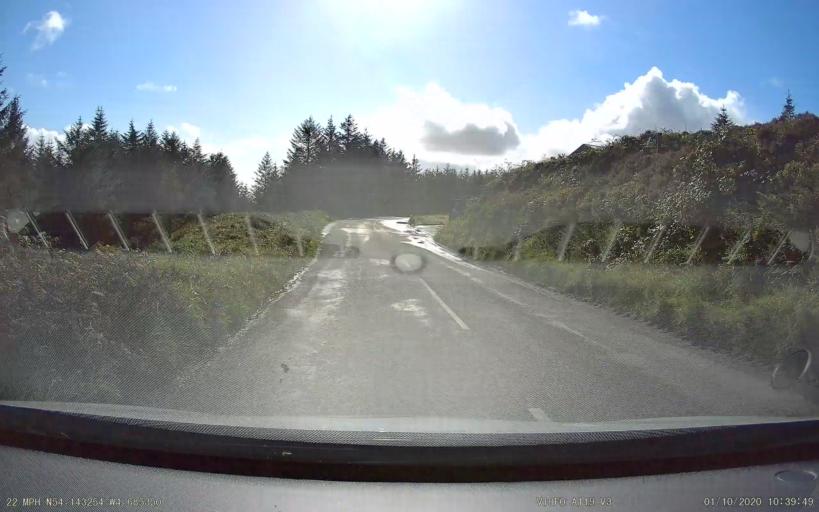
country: IM
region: Castletown
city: Castletown
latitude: 54.1433
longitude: -4.6854
